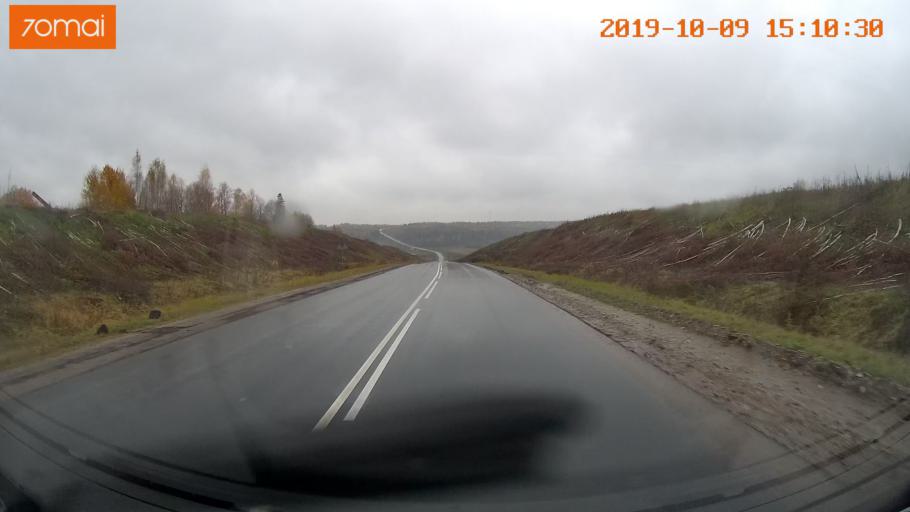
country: RU
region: Kostroma
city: Susanino
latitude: 58.1771
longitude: 41.6403
